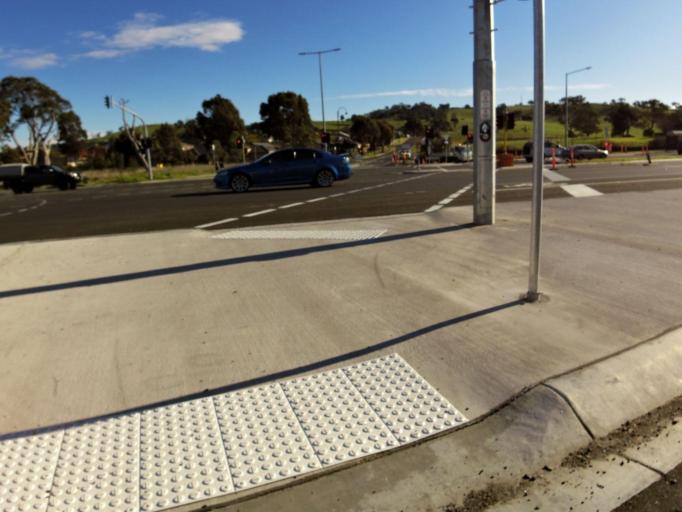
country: AU
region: Victoria
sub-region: Whittlesea
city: Mernda
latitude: -37.6228
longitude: 145.0968
